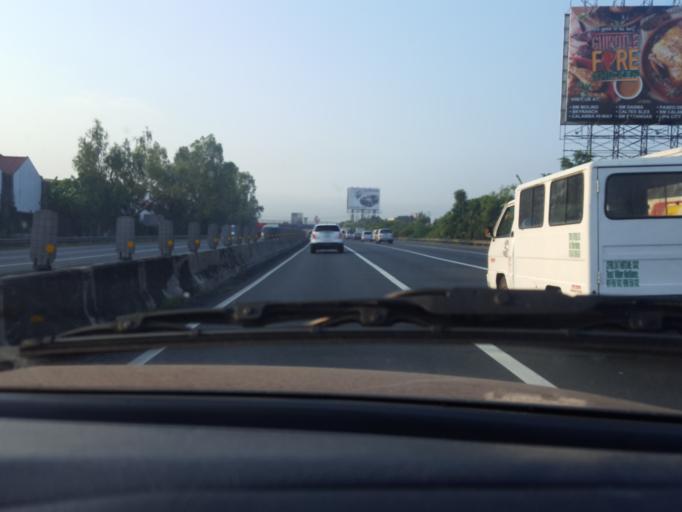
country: PH
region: Calabarzon
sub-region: Province of Laguna
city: San Pedro
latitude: 14.3994
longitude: 121.0390
